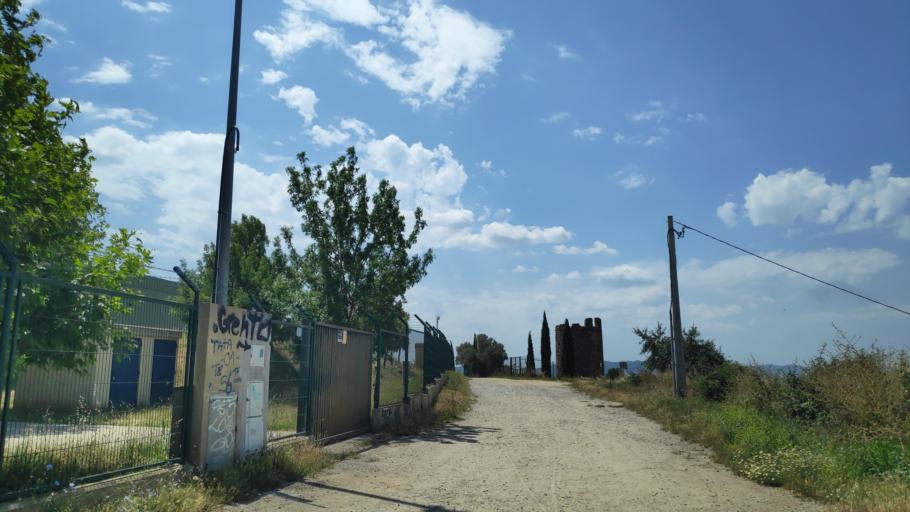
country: ES
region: Catalonia
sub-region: Provincia de Barcelona
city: Les Franqueses del Valles
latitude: 41.6147
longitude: 2.2999
